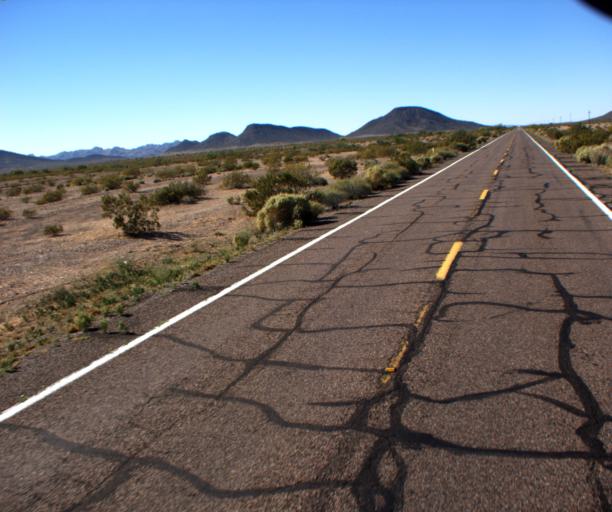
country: US
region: Arizona
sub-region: Maricopa County
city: Gila Bend
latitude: 32.7915
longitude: -112.8044
